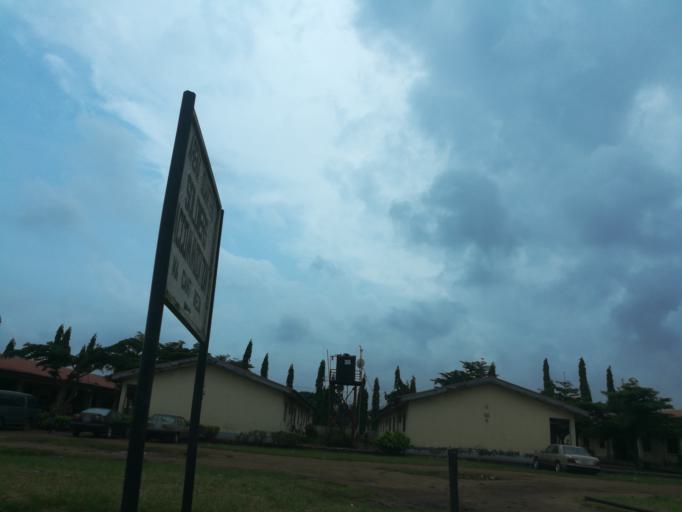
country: NG
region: Lagos
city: Oshodi
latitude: 6.5655
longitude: 3.3512
